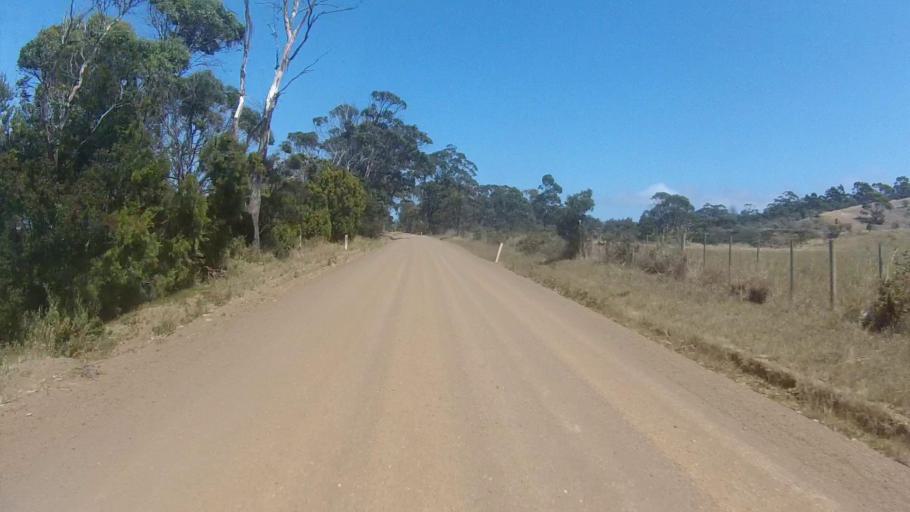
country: AU
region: Tasmania
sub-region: Sorell
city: Sorell
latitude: -42.8318
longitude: 147.8561
